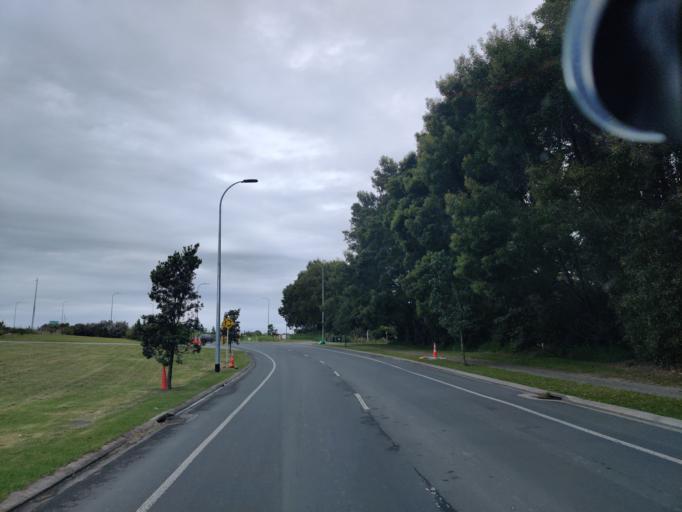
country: NZ
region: Auckland
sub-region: Auckland
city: Rothesay Bay
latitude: -36.6020
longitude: 174.6608
